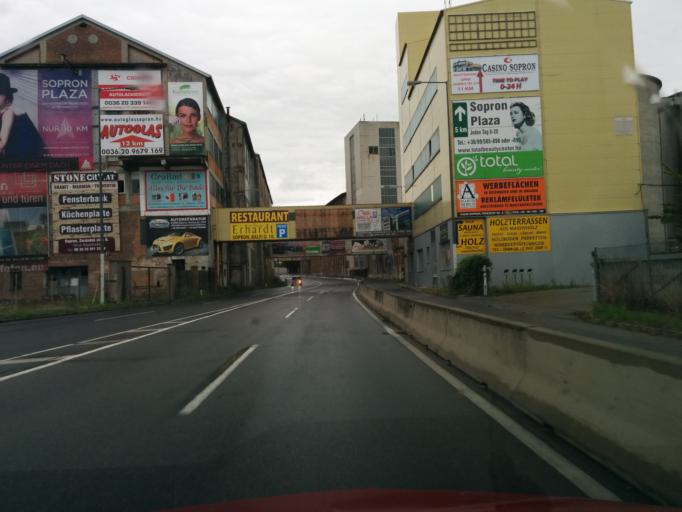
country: AT
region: Burgenland
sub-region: Eisenstadt-Umgebung
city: Zagersdorf
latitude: 47.7713
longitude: 16.5298
